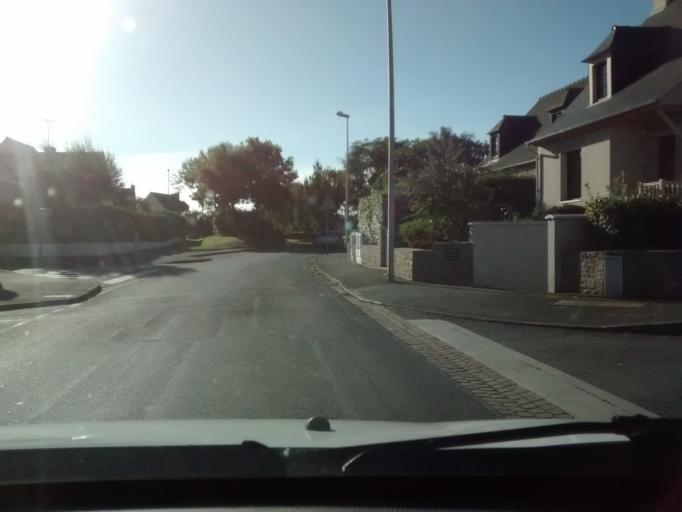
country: FR
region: Brittany
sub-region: Departement d'Ille-et-Vilaine
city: Saint-Malo
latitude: 48.6613
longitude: -1.9717
